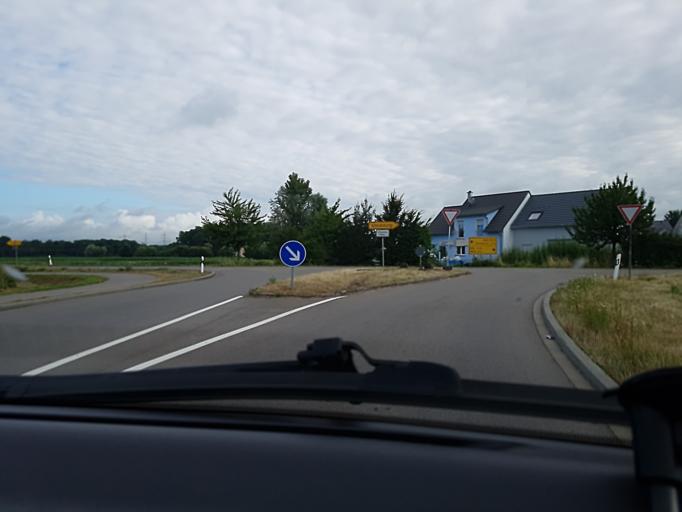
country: DE
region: Baden-Wuerttemberg
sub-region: Freiburg Region
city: Offenburg
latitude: 48.4992
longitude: 7.9149
